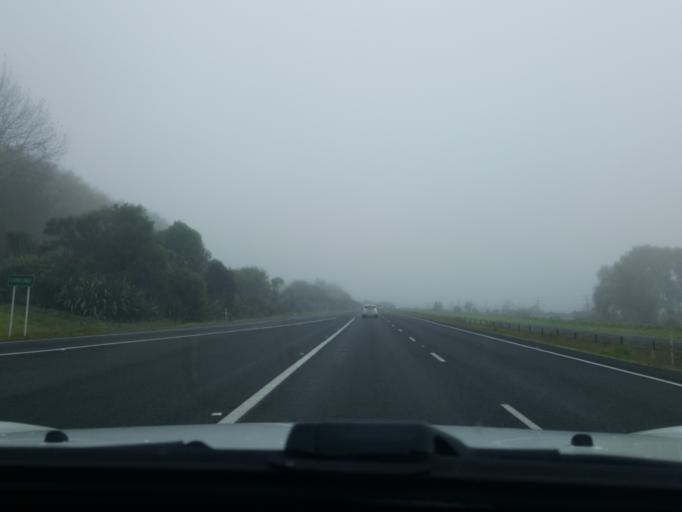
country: NZ
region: Waikato
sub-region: Waikato District
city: Te Kauwhata
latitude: -37.4516
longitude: 175.1530
